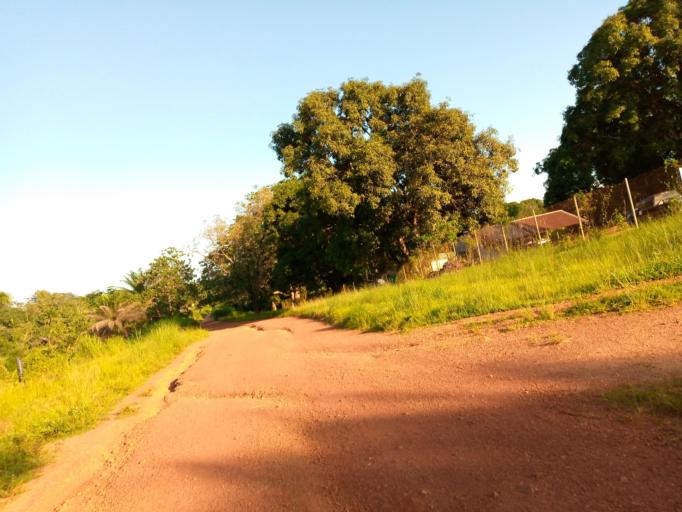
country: SL
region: Northern Province
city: Yonibana
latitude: 8.4502
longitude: -12.2438
